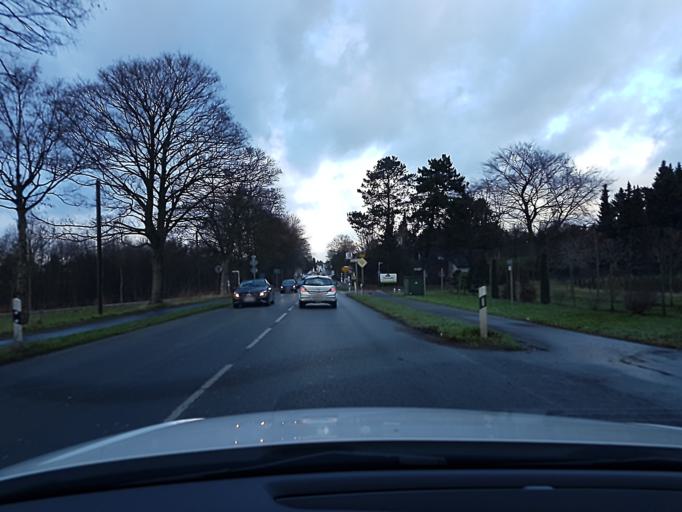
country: DE
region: North Rhine-Westphalia
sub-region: Regierungsbezirk Dusseldorf
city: Ratingen
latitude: 51.3622
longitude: 6.8632
